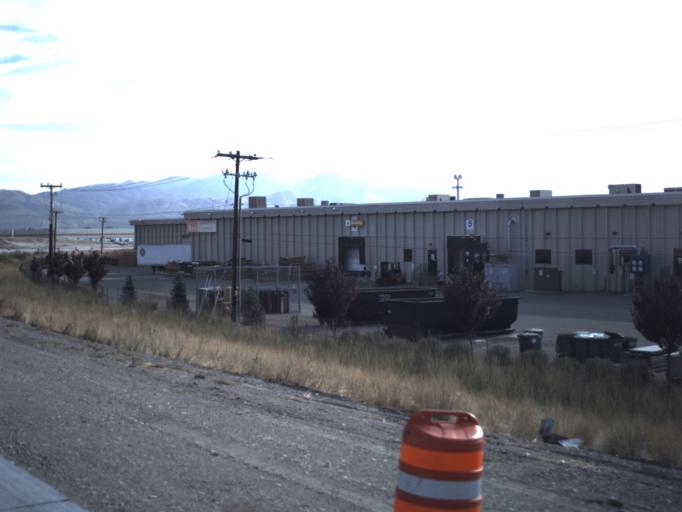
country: US
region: Utah
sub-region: Salt Lake County
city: Taylorsville
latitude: 40.7208
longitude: -111.9524
